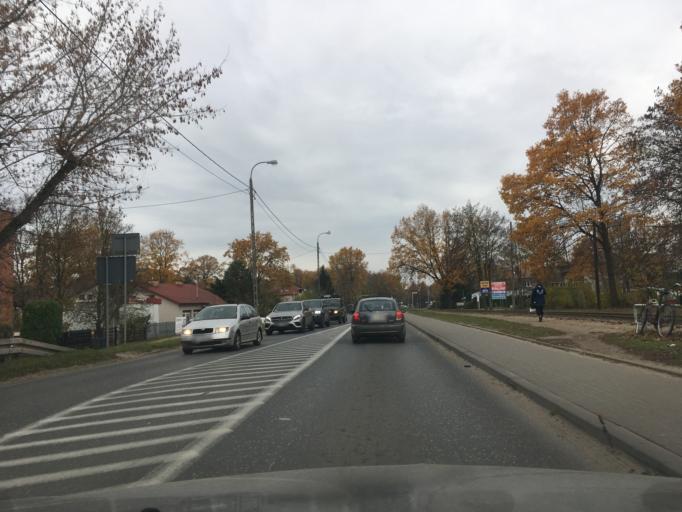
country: PL
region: Masovian Voivodeship
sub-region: Powiat piaseczynski
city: Piaseczno
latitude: 52.0650
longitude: 21.0187
